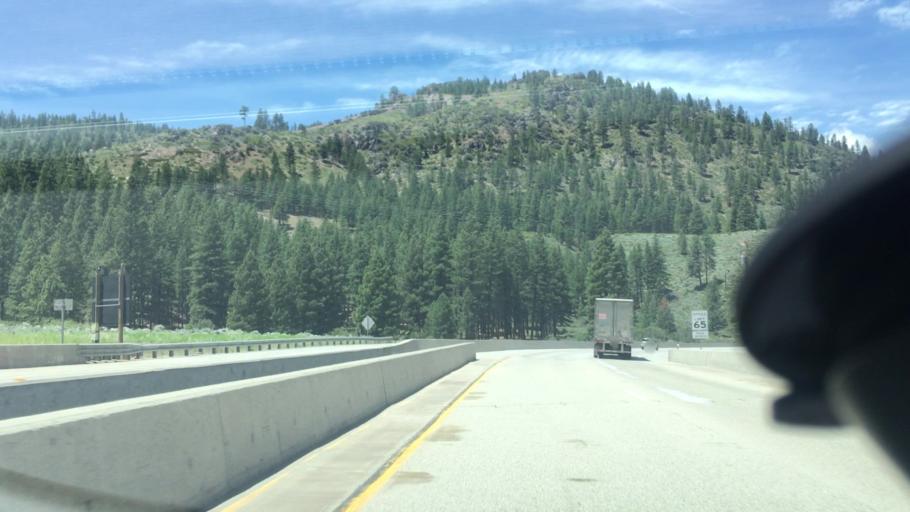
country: US
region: Nevada
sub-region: Washoe County
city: Verdi
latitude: 39.4038
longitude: -120.0250
